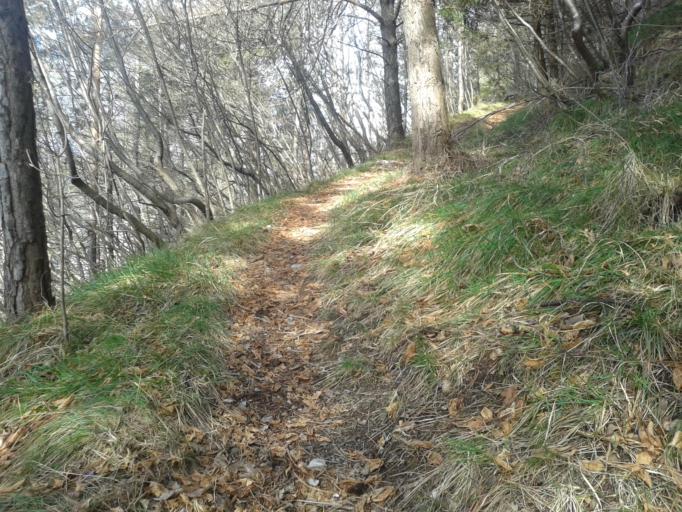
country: IT
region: Trentino-Alto Adige
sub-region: Provincia di Trento
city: Storo
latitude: 45.8398
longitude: 10.5701
